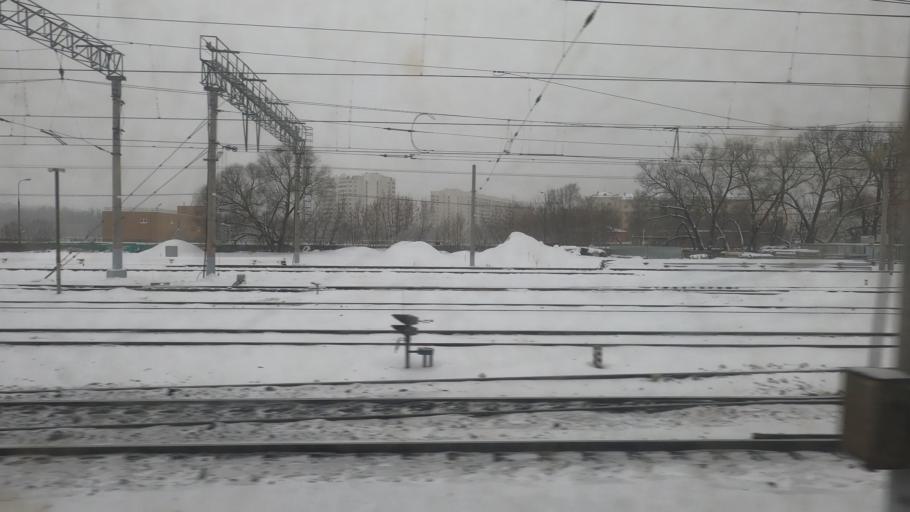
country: RU
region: Moscow
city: Perovo
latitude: 55.7369
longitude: 37.7819
